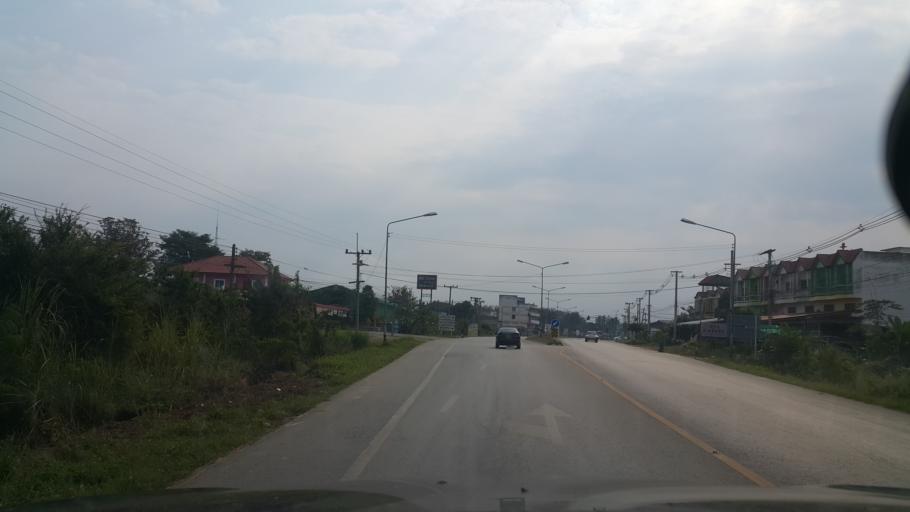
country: TH
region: Sukhothai
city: Si Samrong
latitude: 17.1763
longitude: 99.8498
